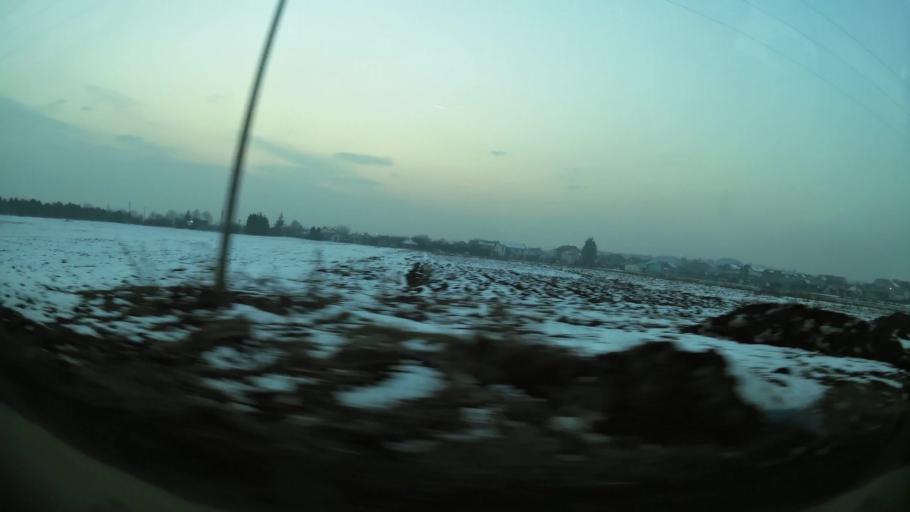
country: MK
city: Creshevo
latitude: 42.0087
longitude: 21.5173
